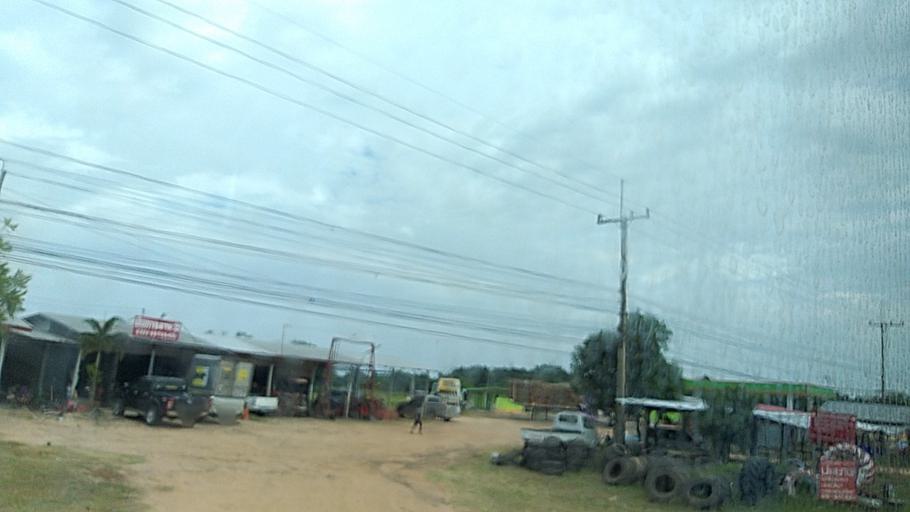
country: TH
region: Kalasin
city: Khong Chai
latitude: 16.1350
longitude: 103.4494
